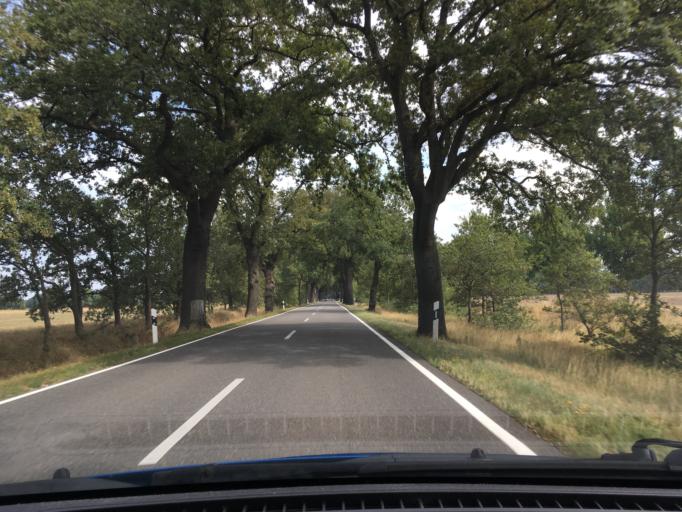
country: DE
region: Mecklenburg-Vorpommern
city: Eldena
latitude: 53.2490
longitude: 11.4349
